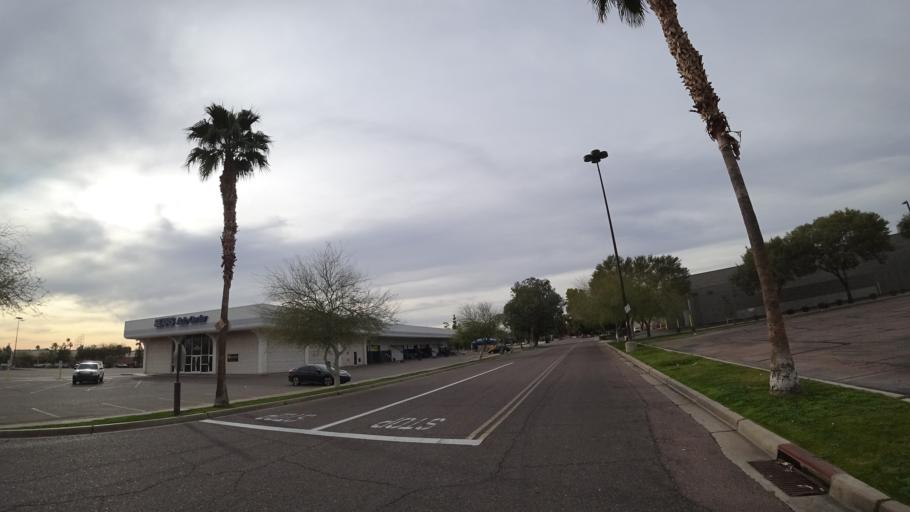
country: US
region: Arizona
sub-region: Maricopa County
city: Glendale
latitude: 33.5781
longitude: -112.1230
